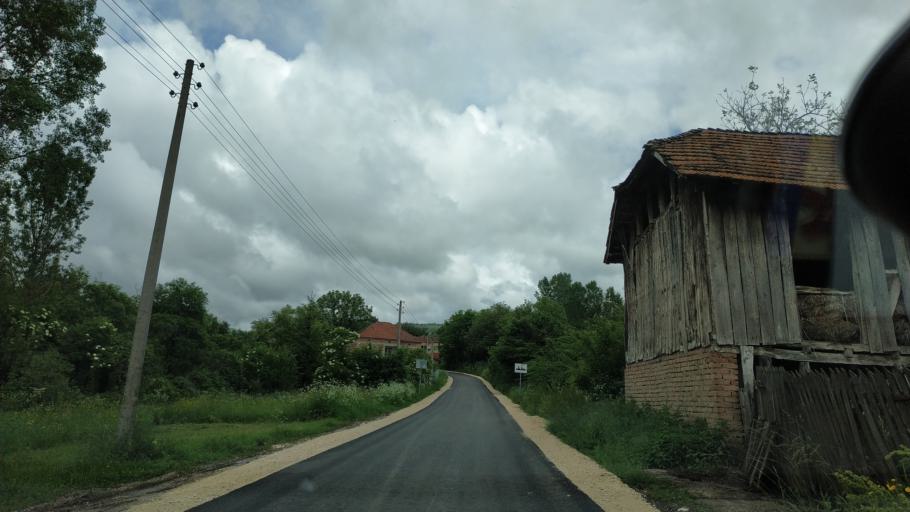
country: RS
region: Central Serbia
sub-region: Zajecarski Okrug
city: Soko Banja
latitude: 43.6706
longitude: 21.9131
